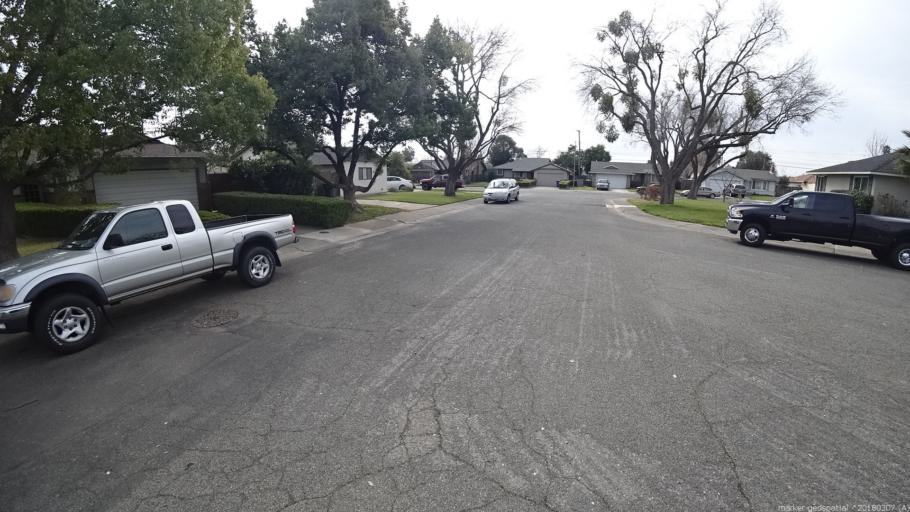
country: US
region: California
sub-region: Sacramento County
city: Parkway
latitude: 38.5263
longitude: -121.4531
